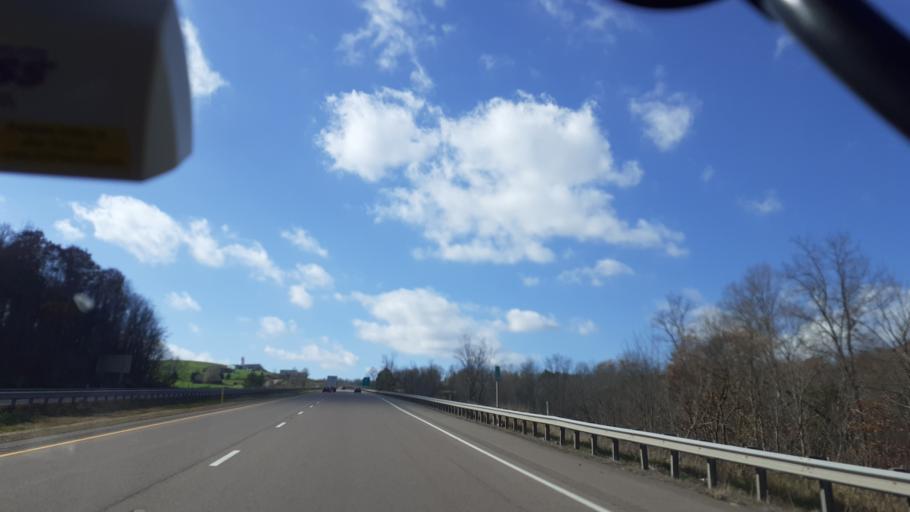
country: US
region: Pennsylvania
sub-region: Somerset County
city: Meyersdale
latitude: 39.6944
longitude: -79.1412
